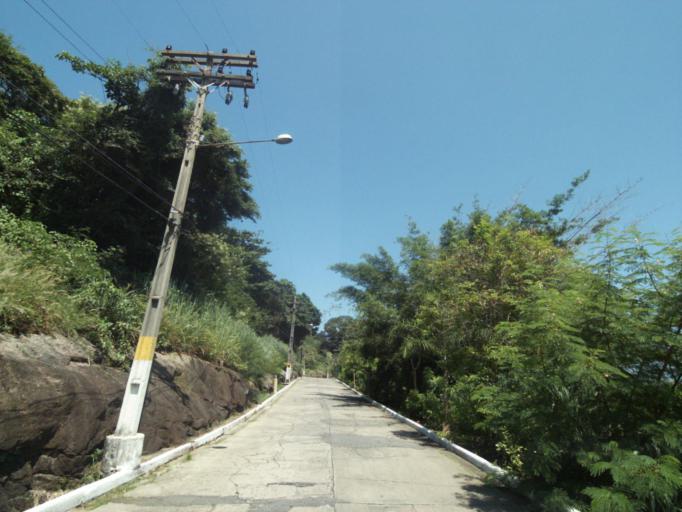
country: BR
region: Rio de Janeiro
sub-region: Niteroi
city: Niteroi
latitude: -22.9360
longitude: -43.1276
